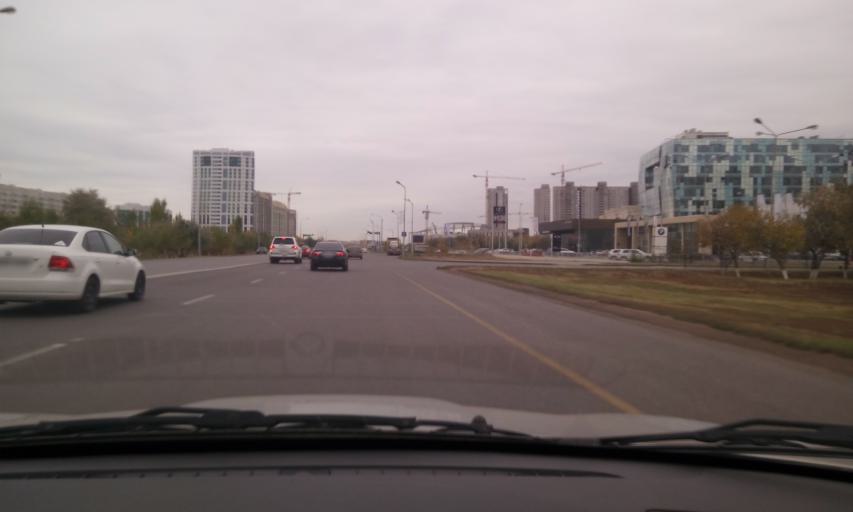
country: KZ
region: Astana Qalasy
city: Astana
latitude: 51.1209
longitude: 71.4120
